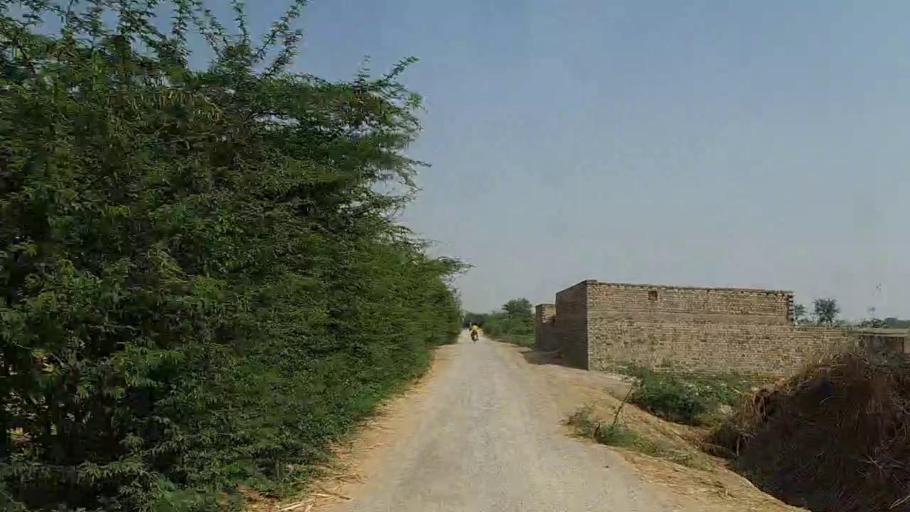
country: PK
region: Sindh
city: Naukot
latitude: 24.7778
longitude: 69.3553
